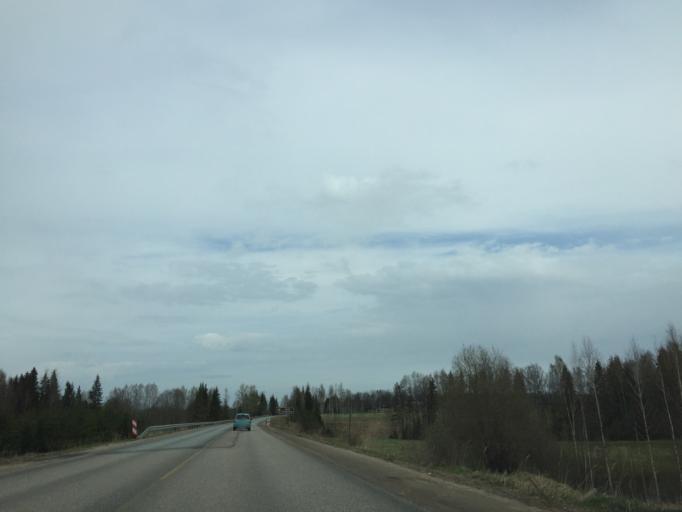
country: LV
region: Amatas Novads
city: Drabesi
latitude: 57.2293
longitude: 25.2545
